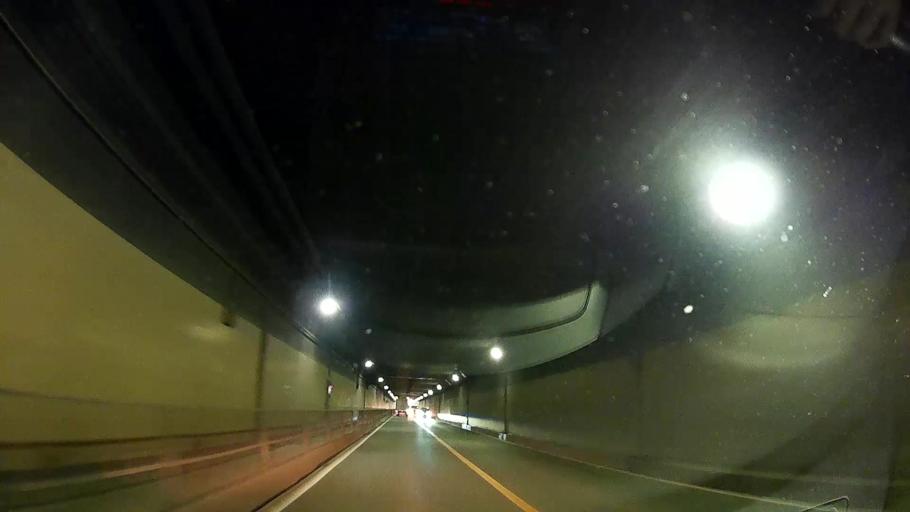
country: JP
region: Kumamoto
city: Ozu
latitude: 32.8361
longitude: 130.8545
